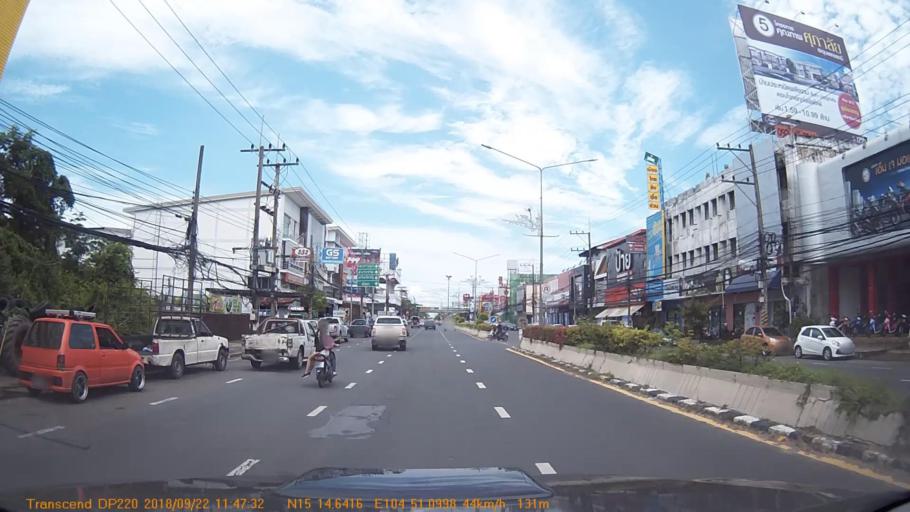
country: TH
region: Changwat Ubon Ratchathani
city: Ubon Ratchathani
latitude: 15.2438
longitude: 104.8517
